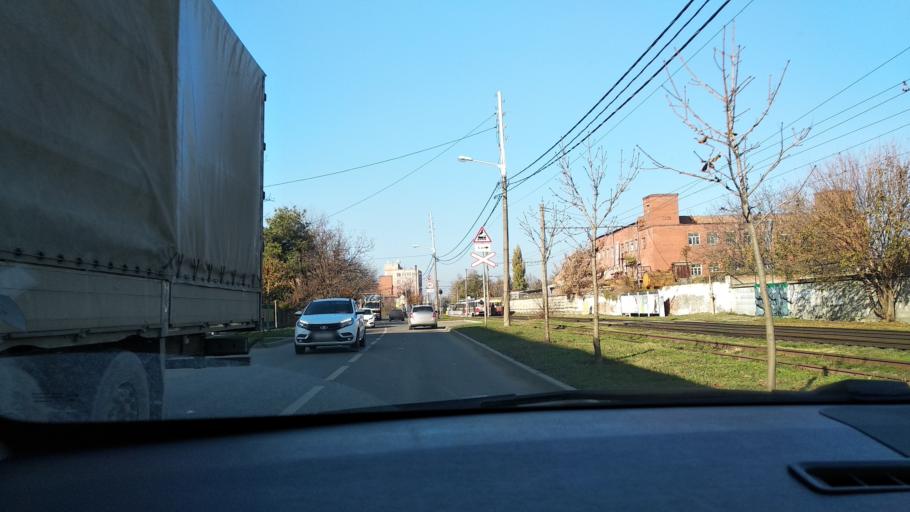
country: RU
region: Krasnodarskiy
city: Krasnodar
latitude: 45.0053
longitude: 39.0182
